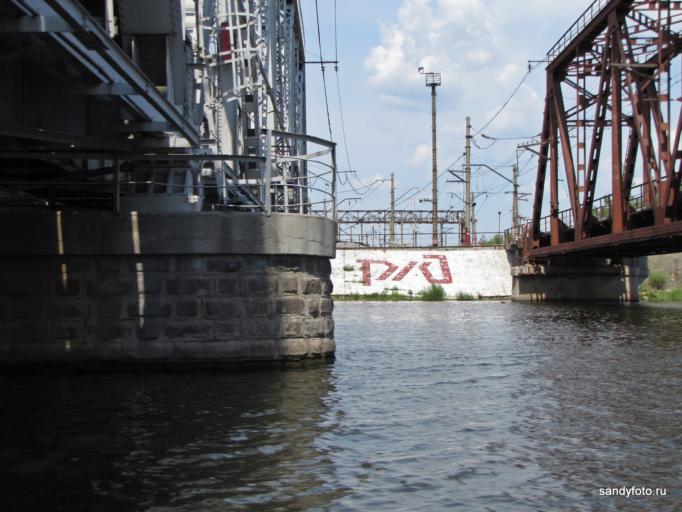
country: RU
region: Chelyabinsk
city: Troitsk
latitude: 54.0554
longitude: 61.6114
